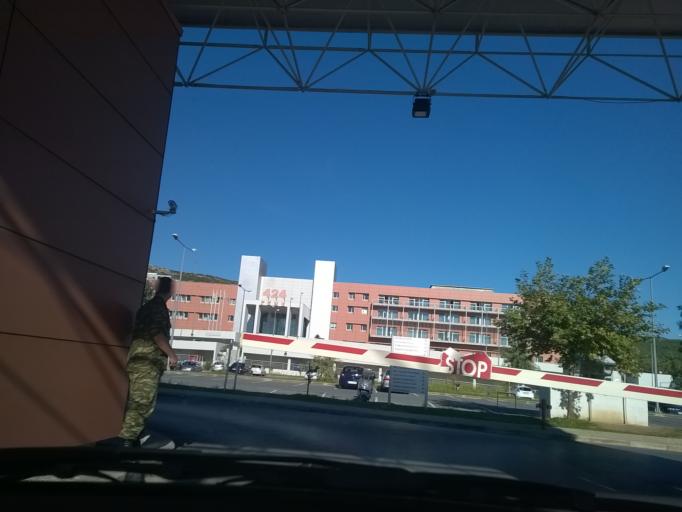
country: GR
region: Central Macedonia
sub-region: Nomos Thessalonikis
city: Polichni
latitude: 40.6723
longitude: 22.9619
